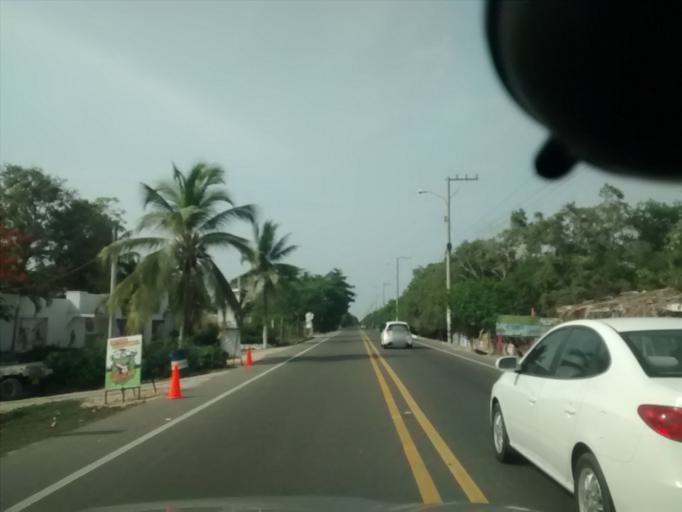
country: CO
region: Bolivar
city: Cartagena
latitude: 10.4690
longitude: -75.4977
